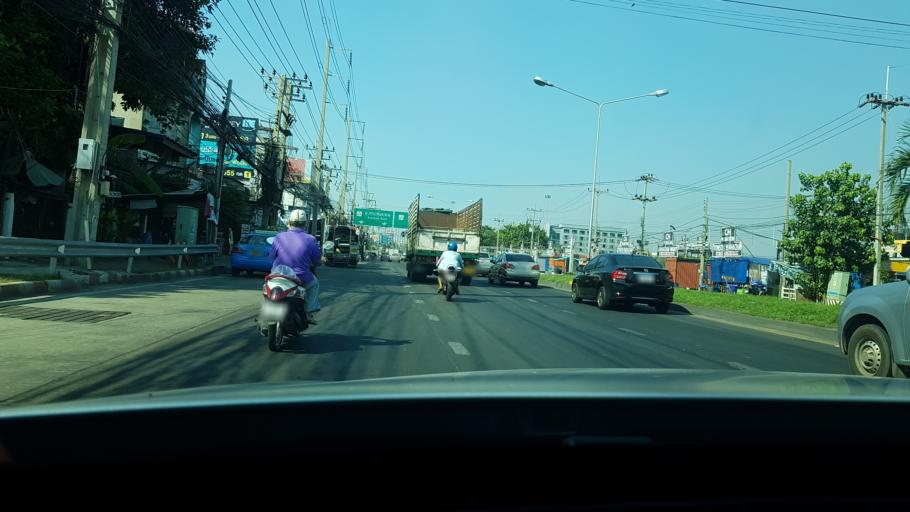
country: TH
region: Samut Sakhon
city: Samut Sakhon
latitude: 13.5594
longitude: 100.2722
